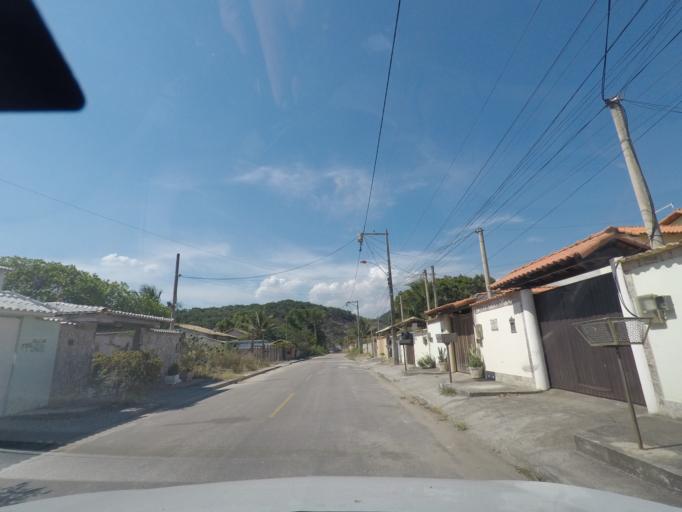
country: BR
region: Rio de Janeiro
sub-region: Niteroi
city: Niteroi
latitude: -22.9606
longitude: -42.9703
